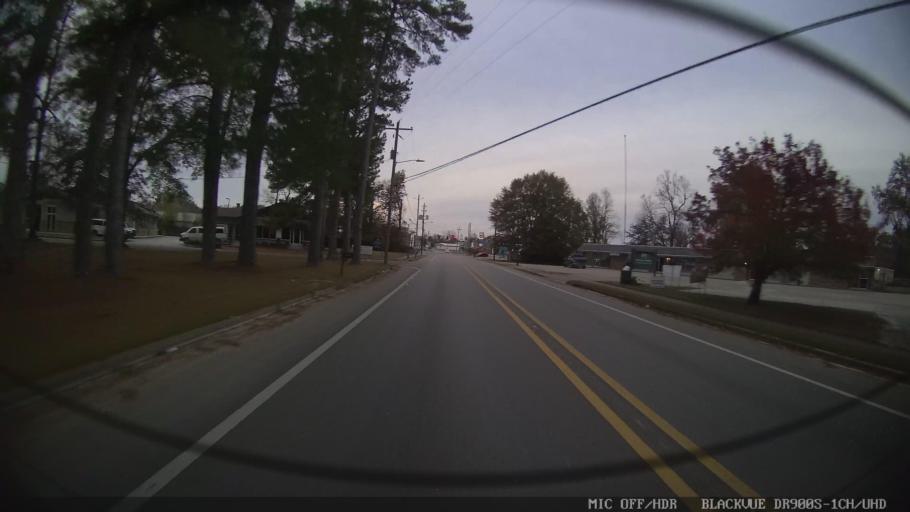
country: US
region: Mississippi
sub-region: Clarke County
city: Quitman
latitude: 32.0373
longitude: -88.7267
